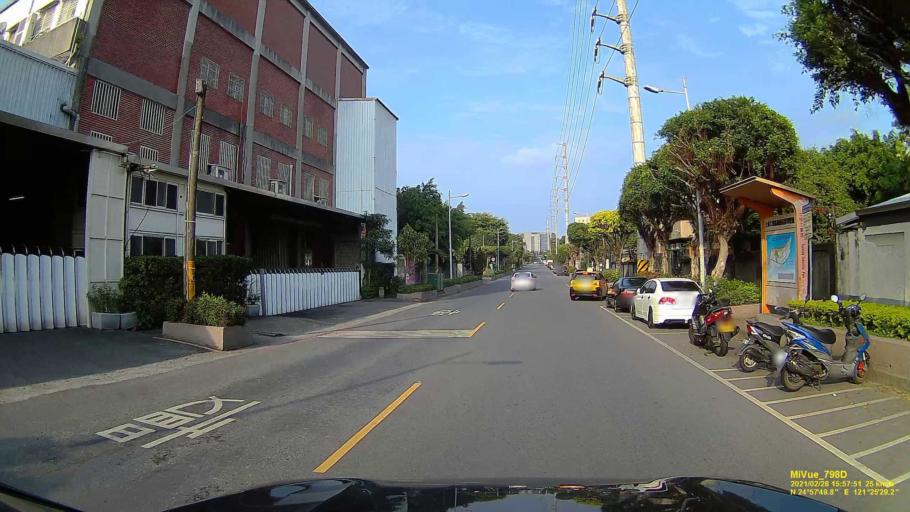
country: TW
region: Taipei
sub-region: Taipei
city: Banqiao
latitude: 24.9639
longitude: 121.4249
